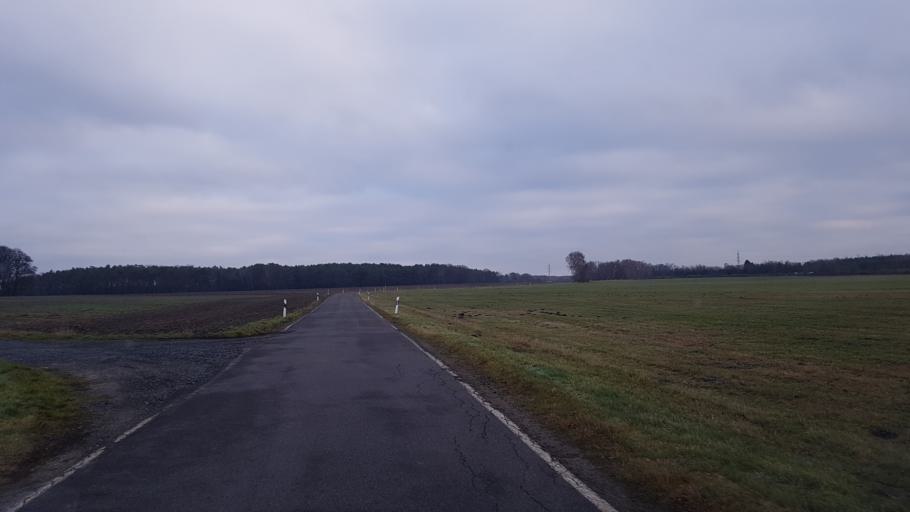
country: DE
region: Brandenburg
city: Schipkau
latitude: 51.5467
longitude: 13.9011
